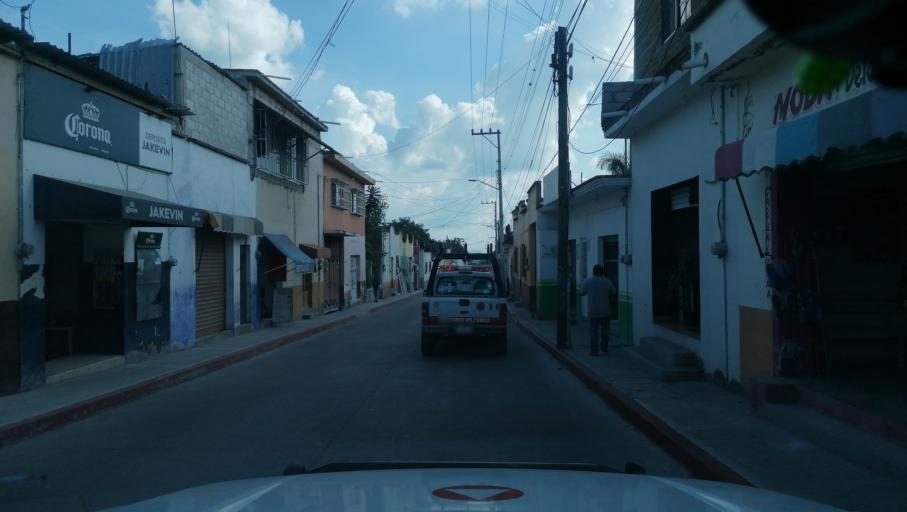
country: MX
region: Morelos
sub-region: Ayala
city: Ciudad Ayala
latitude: 18.7643
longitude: -98.9837
